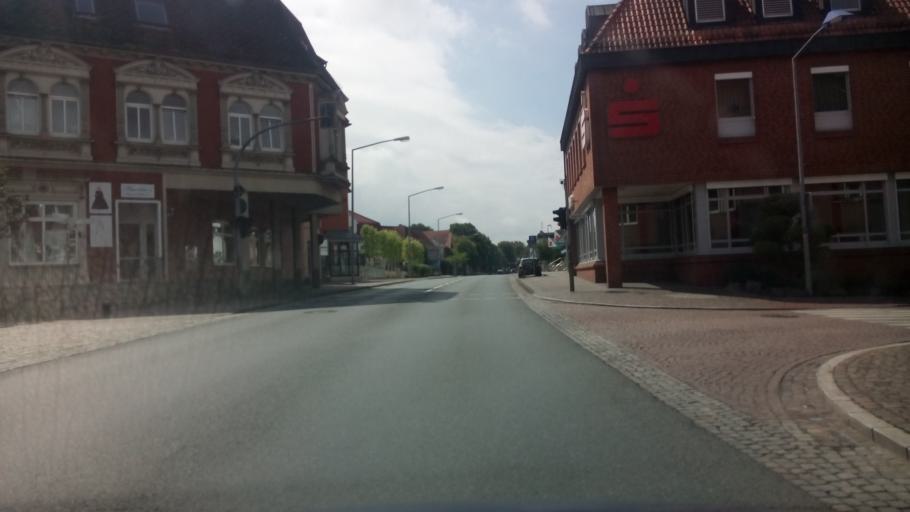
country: DE
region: Lower Saxony
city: Twistringen
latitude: 52.8004
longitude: 8.6390
